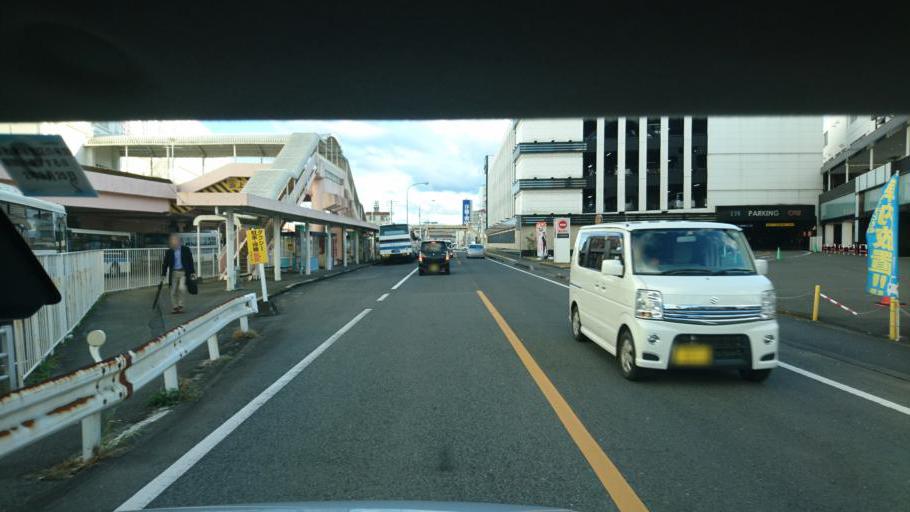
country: JP
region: Miyazaki
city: Miyazaki-shi
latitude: 31.8952
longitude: 131.4188
